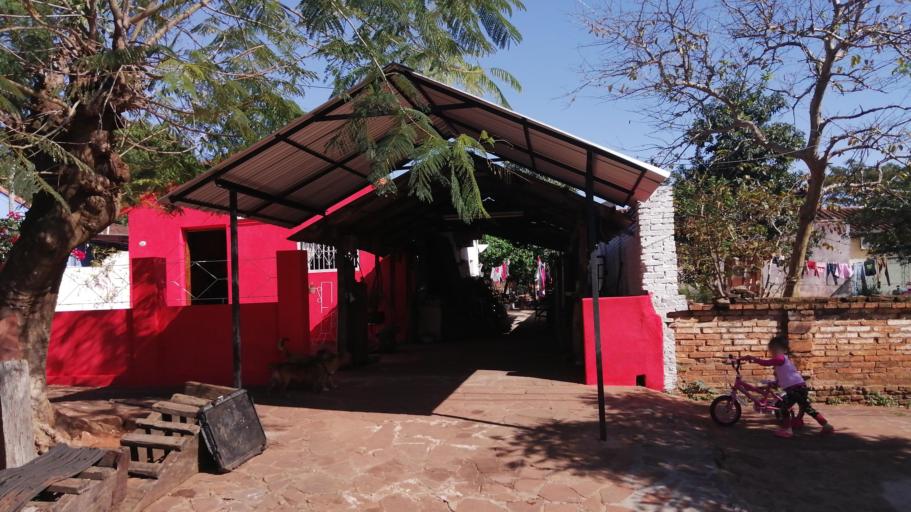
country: PY
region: Misiones
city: San Juan Bautista
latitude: -26.6661
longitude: -57.1389
